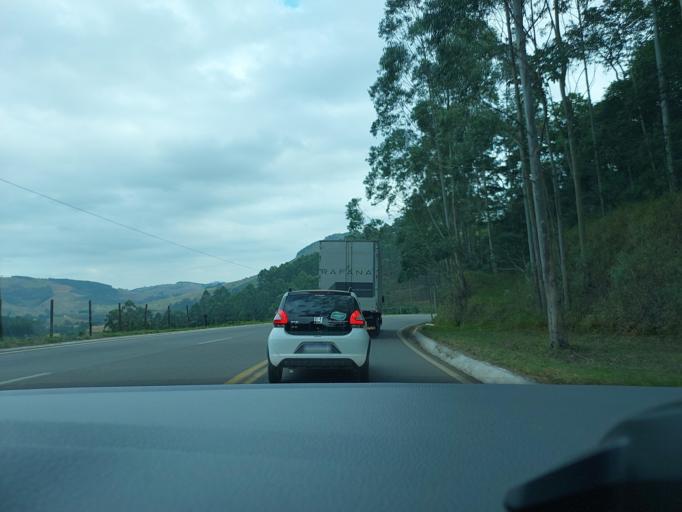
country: BR
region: Minas Gerais
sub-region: Mirai
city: Mirai
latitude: -20.9655
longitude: -42.5913
